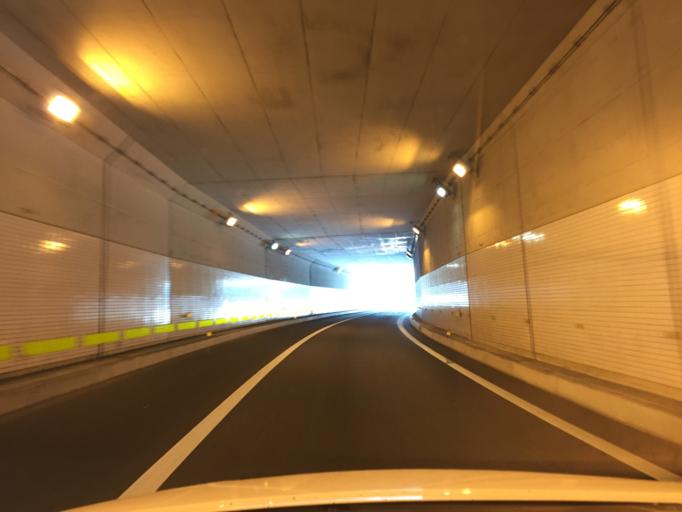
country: JP
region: Fukushima
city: Funehikimachi-funehiki
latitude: 37.2929
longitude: 140.6200
